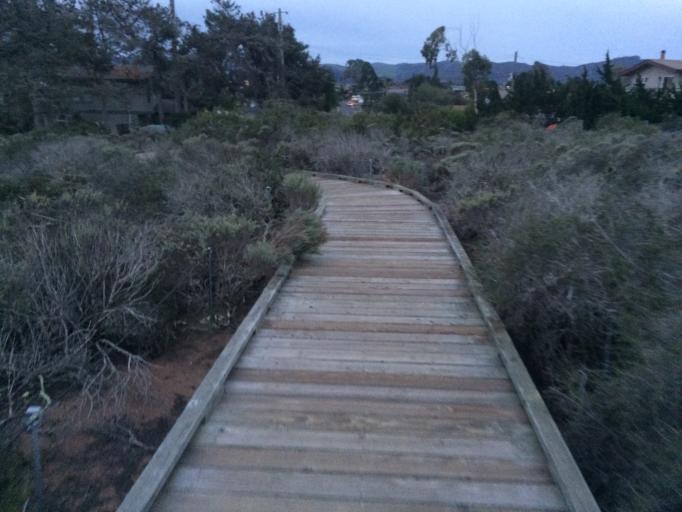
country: US
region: California
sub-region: San Luis Obispo County
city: Los Osos
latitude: 35.3321
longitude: -120.8254
